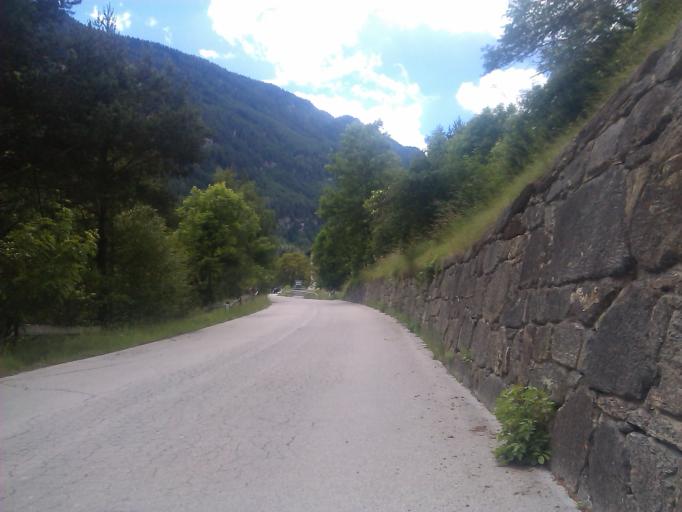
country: AT
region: Tyrol
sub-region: Politischer Bezirk Landeck
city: Serfaus
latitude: 47.0121
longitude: 10.5981
